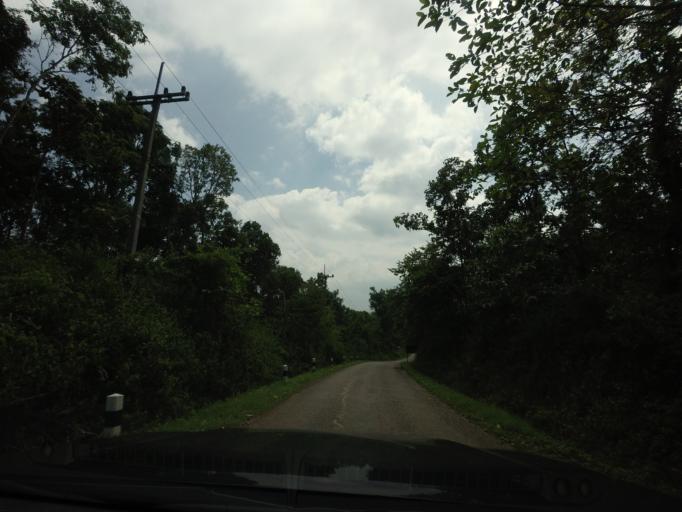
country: TH
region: Loei
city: Phu Ruea
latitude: 17.4633
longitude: 101.3557
